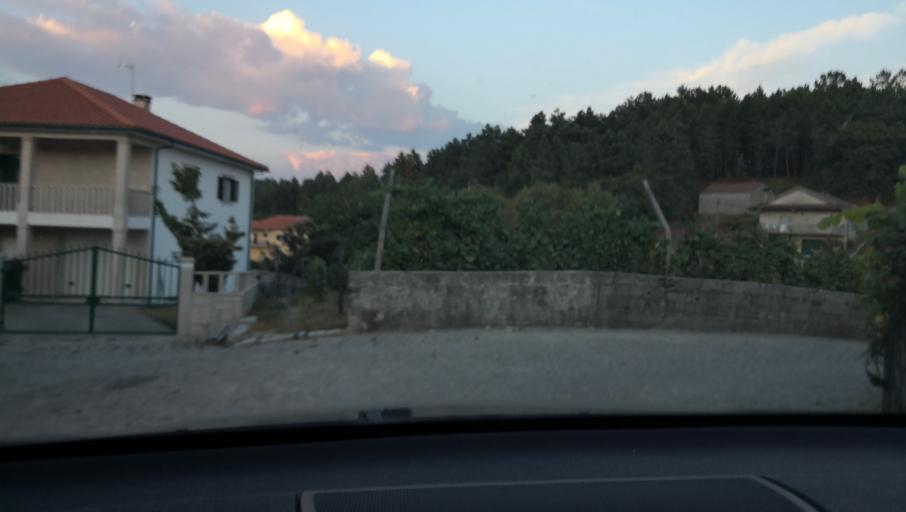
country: PT
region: Vila Real
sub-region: Sabrosa
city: Vilela
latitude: 41.2364
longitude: -7.6154
